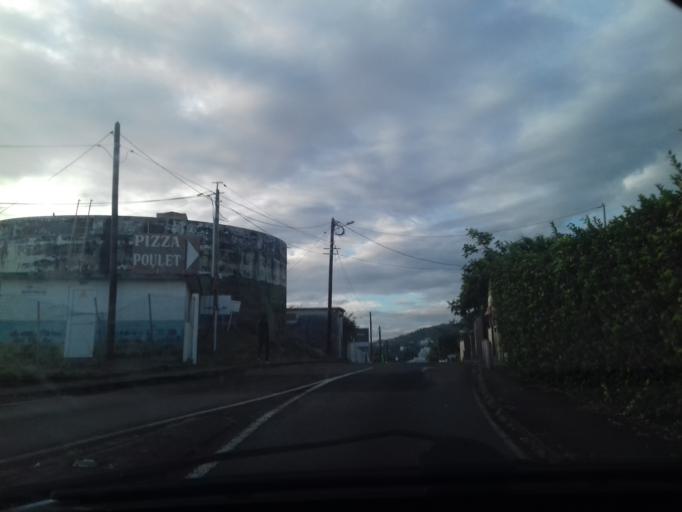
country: MQ
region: Martinique
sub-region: Martinique
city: Fort-de-France
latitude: 14.6165
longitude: -61.0868
